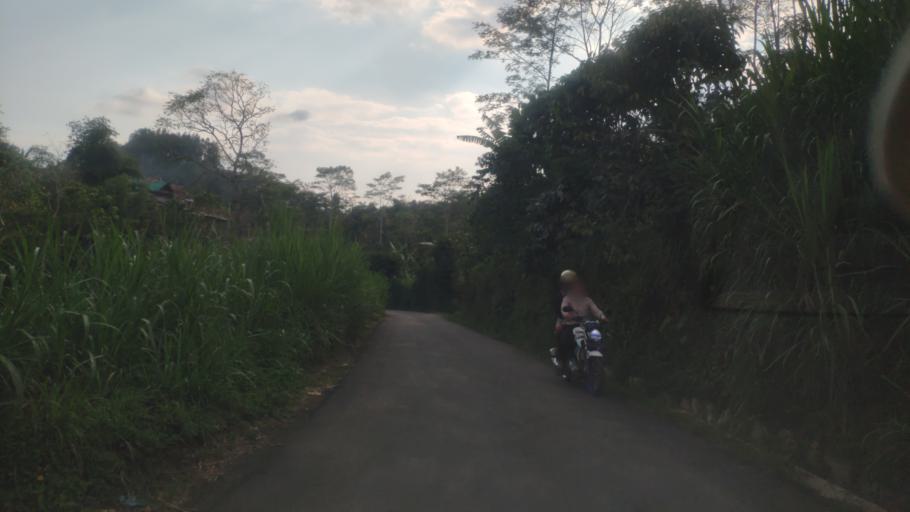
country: ID
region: Central Java
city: Wonosobo
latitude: -7.2410
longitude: 109.7030
